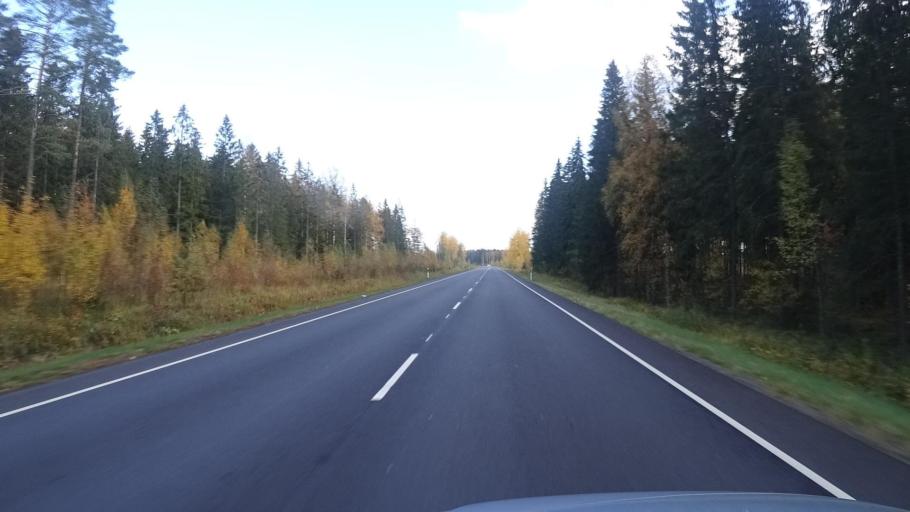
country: FI
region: Satakunta
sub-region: Rauma
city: Eura
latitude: 61.1112
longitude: 22.2058
